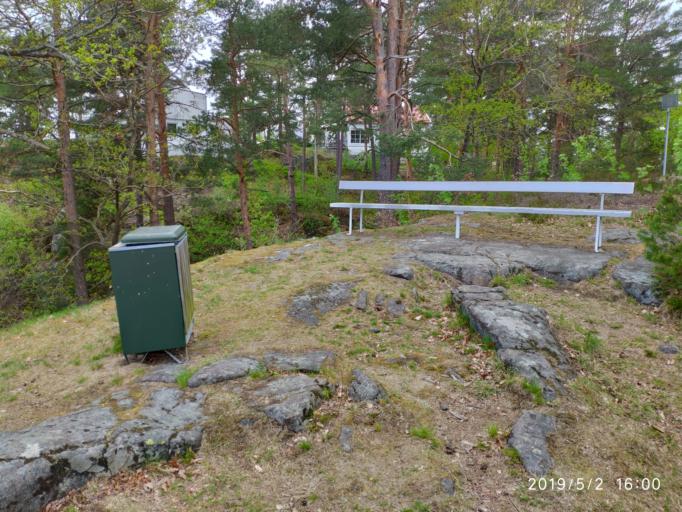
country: NO
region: Telemark
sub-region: Kragero
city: Kragero
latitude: 58.8699
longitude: 9.4095
